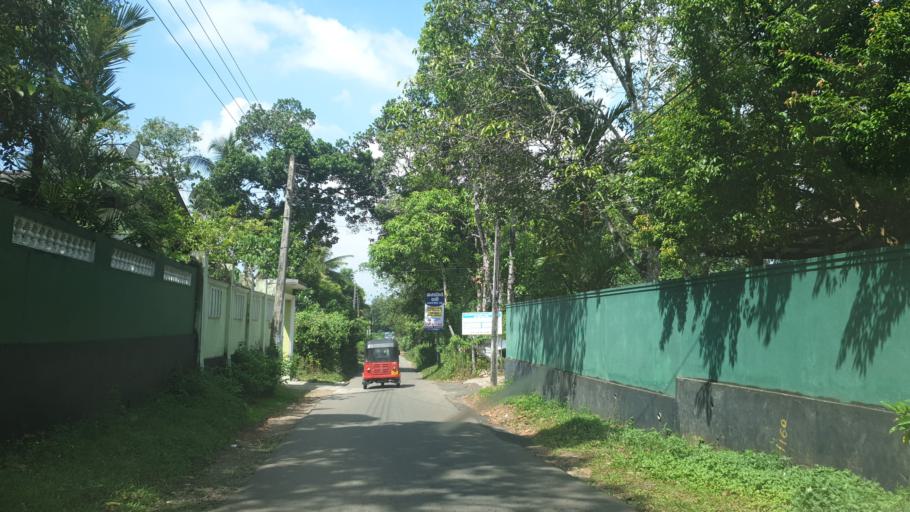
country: LK
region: Western
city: Horana South
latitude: 6.7005
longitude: 79.9863
